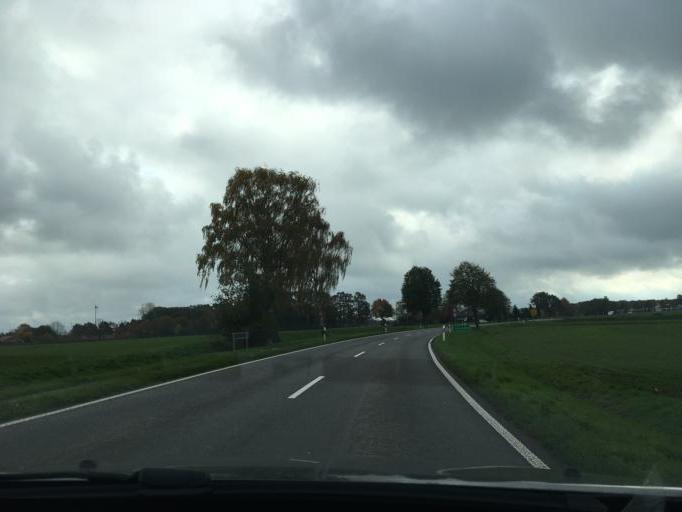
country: DE
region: North Rhine-Westphalia
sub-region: Regierungsbezirk Munster
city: Vreden
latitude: 52.0848
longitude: 6.7796
